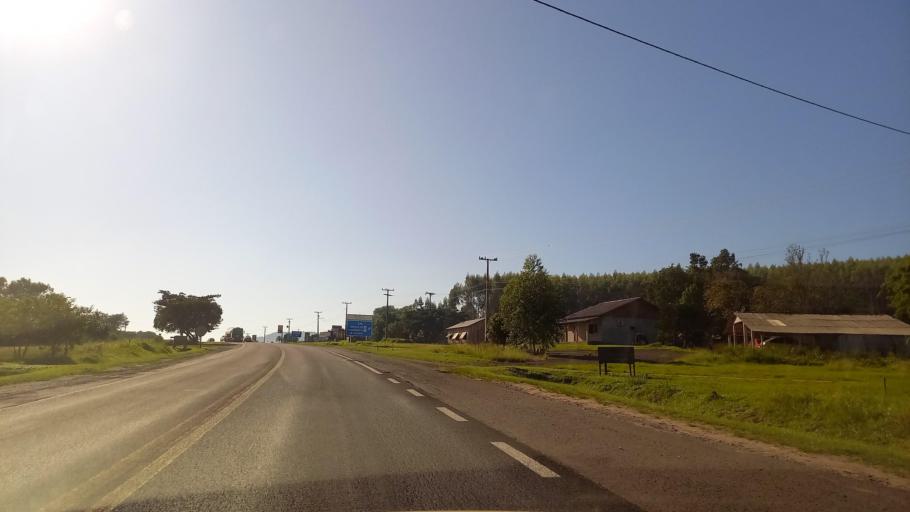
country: BR
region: Rio Grande do Sul
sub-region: Taquari
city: Taquari
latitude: -29.7108
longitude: -51.7684
